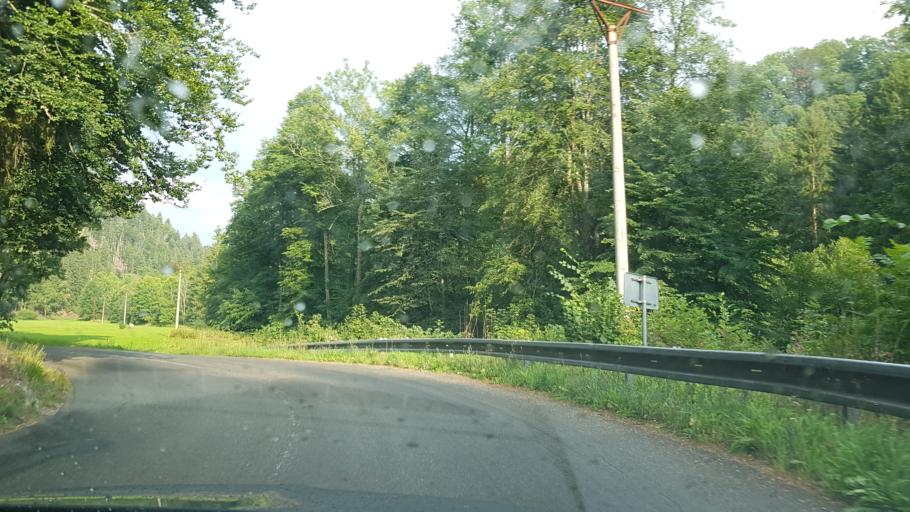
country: CZ
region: Olomoucky
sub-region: Okres Sumperk
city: Hanusovice
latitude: 50.0893
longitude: 16.8790
